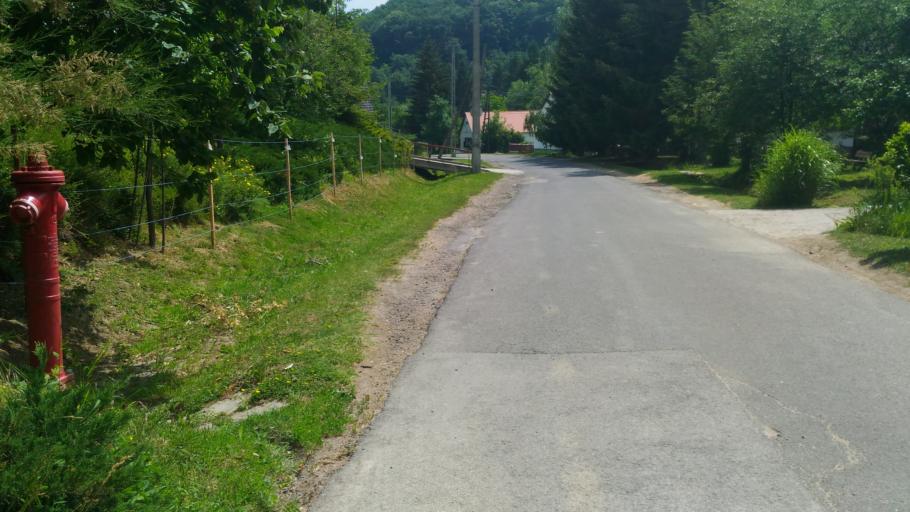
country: HU
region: Baranya
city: Mecseknadasd
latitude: 46.2205
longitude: 18.4115
